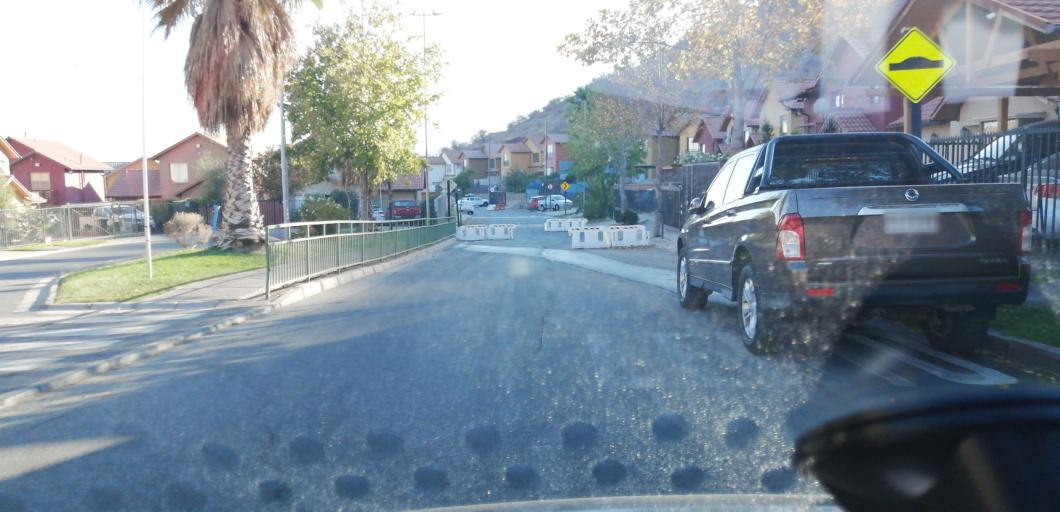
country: CL
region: Santiago Metropolitan
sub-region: Provincia de Santiago
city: Lo Prado
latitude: -33.4548
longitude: -70.8452
